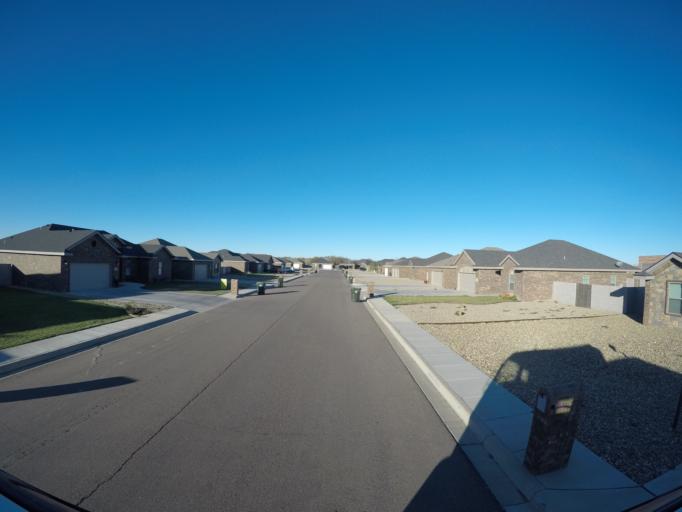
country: US
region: New Mexico
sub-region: Curry County
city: Clovis
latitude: 34.4090
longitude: -103.1716
